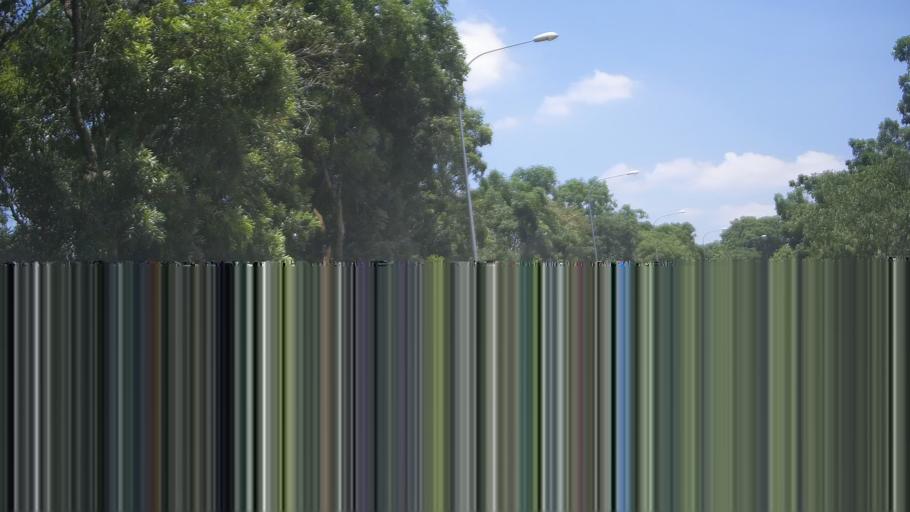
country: MY
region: Johor
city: Johor Bahru
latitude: 1.3638
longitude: 103.7081
